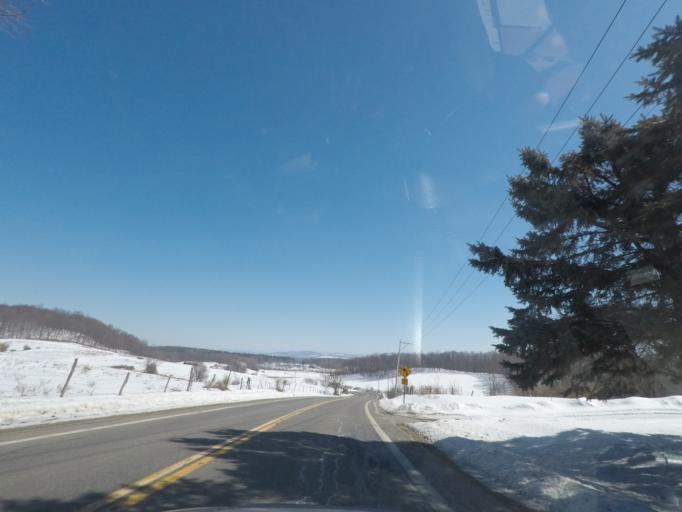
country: US
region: New York
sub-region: Saratoga County
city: Stillwater
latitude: 43.0240
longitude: -73.6682
